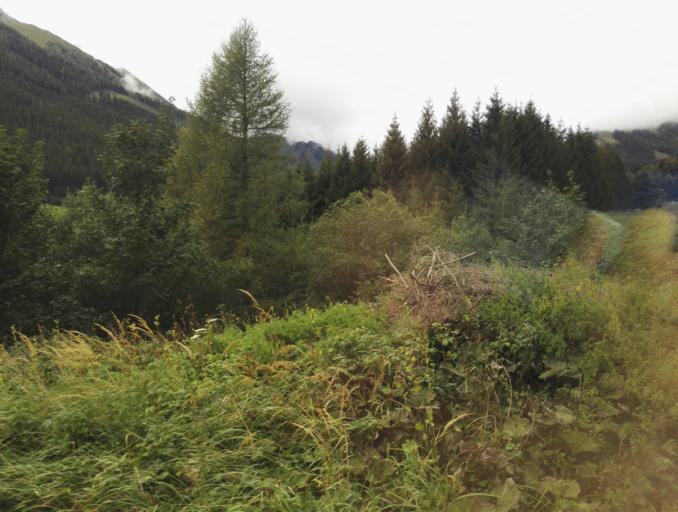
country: AT
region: Styria
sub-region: Politischer Bezirk Leoben
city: Vordernberg
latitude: 47.5055
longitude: 14.9869
